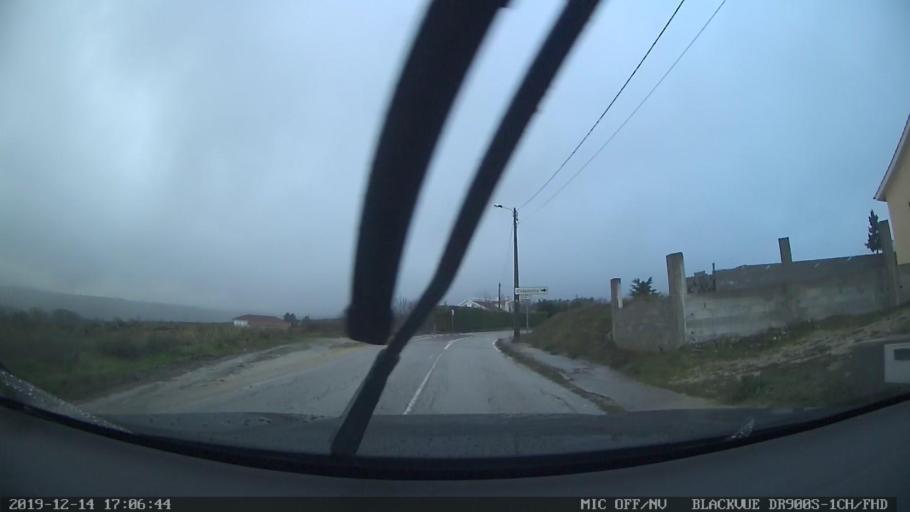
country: PT
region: Vila Real
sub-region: Vila Pouca de Aguiar
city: Vila Pouca de Aguiar
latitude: 41.4572
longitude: -7.5948
